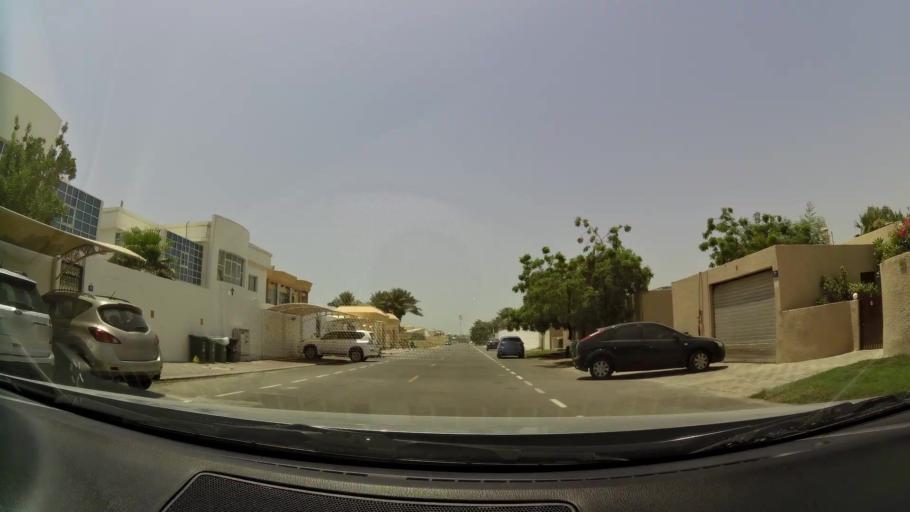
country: AE
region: Dubai
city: Dubai
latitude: 25.1716
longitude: 55.2233
